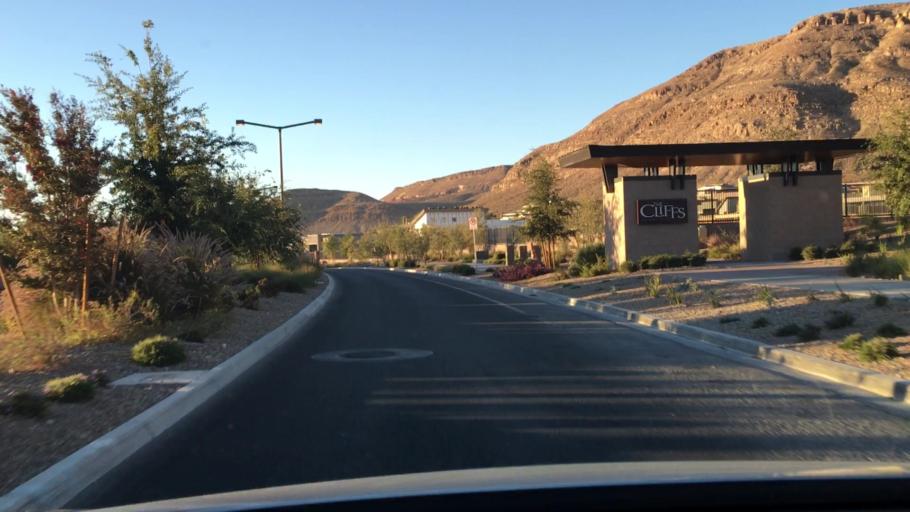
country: US
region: Nevada
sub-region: Clark County
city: Summerlin South
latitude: 36.0792
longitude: -115.3205
